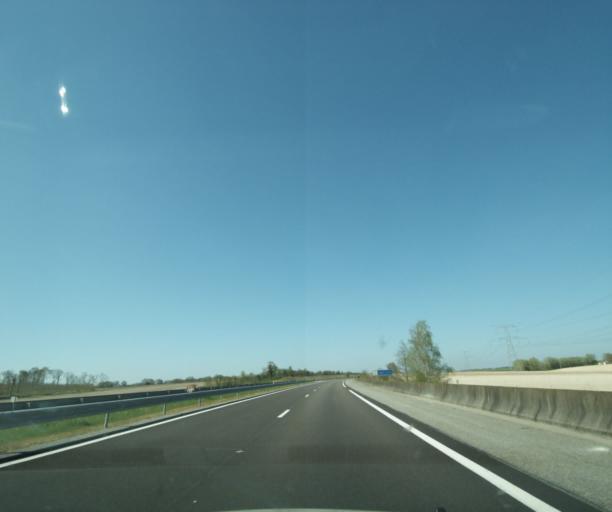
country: FR
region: Bourgogne
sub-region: Departement de la Nievre
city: Neuvy-sur-Loire
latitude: 47.5530
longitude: 2.8854
